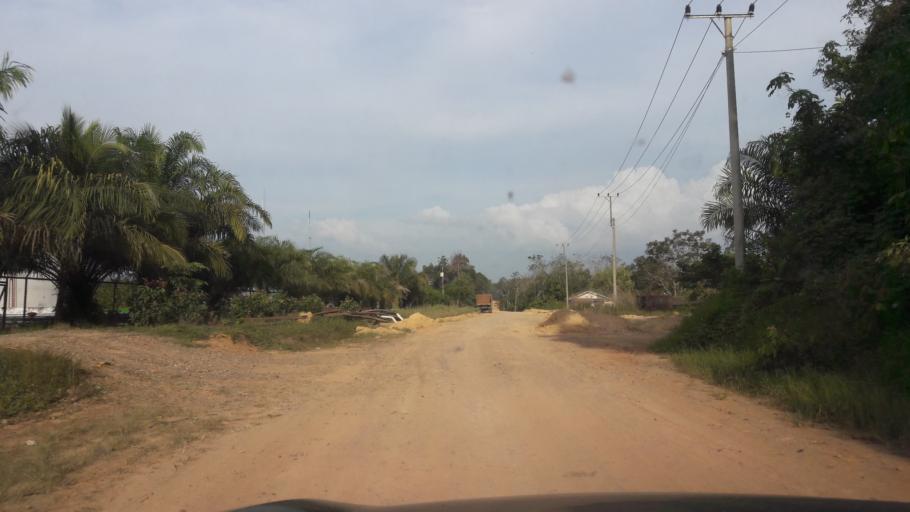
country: ID
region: South Sumatra
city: Gunungmenang
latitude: -3.2642
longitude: 104.0382
